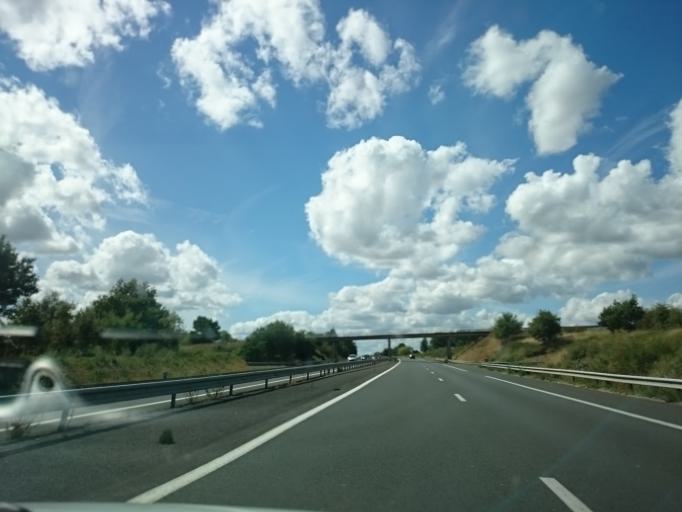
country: FR
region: Pays de la Loire
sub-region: Departement de Maine-et-Loire
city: Ingrandes
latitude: 47.4279
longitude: -0.9143
